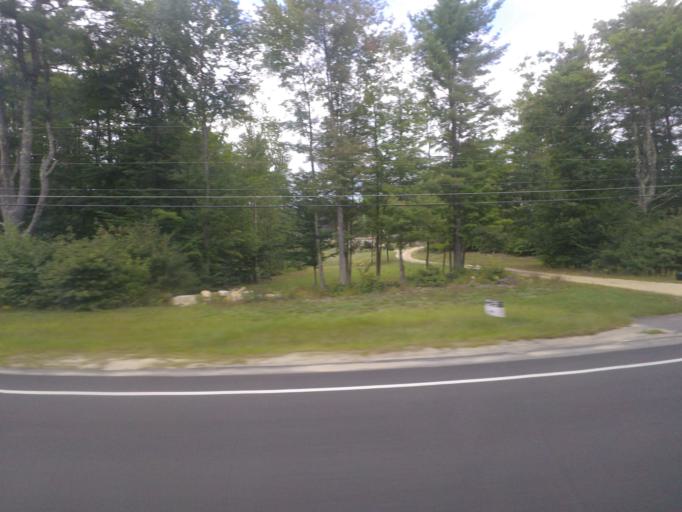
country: US
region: New Hampshire
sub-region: Strafford County
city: Barrington
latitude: 43.2042
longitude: -71.0968
